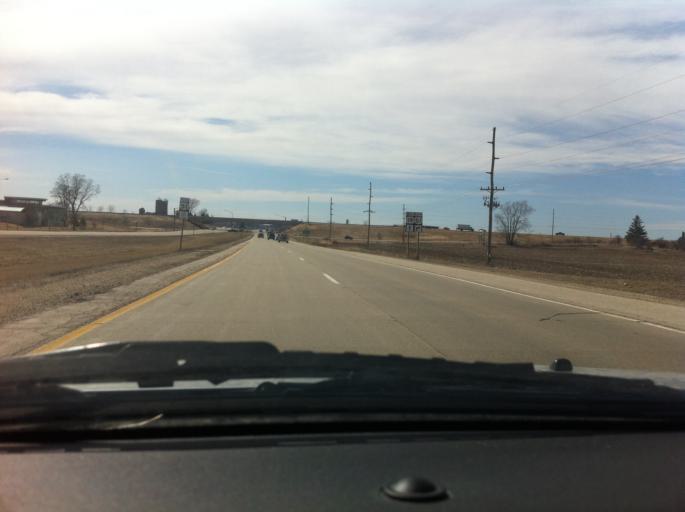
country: US
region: Wisconsin
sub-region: Dane County
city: Windsor
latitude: 43.1949
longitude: -89.3194
